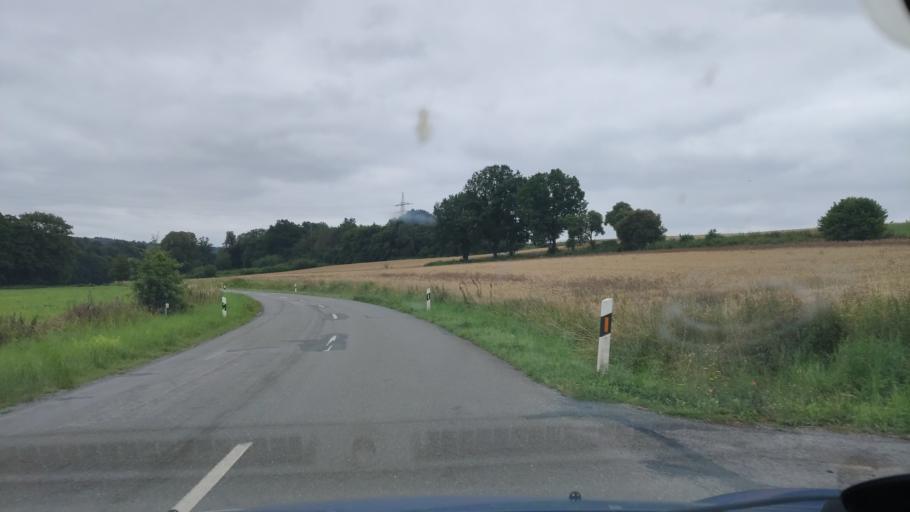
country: DE
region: Lower Saxony
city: Holzminden
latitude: 51.8163
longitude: 9.4750
